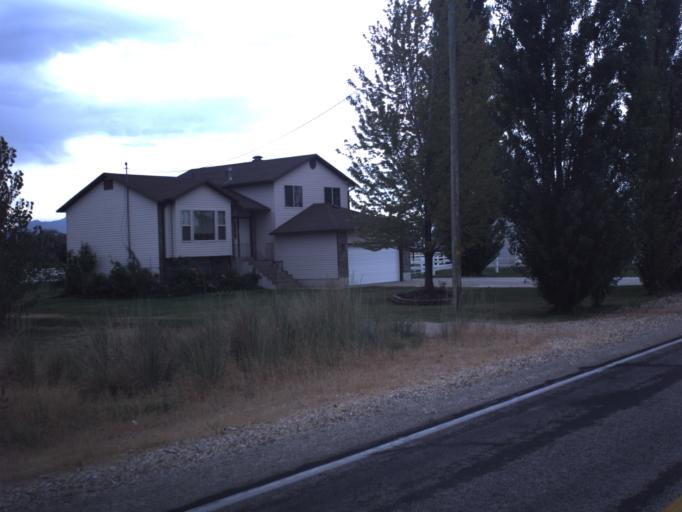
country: US
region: Utah
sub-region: Davis County
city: West Point
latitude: 41.1320
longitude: -112.1126
